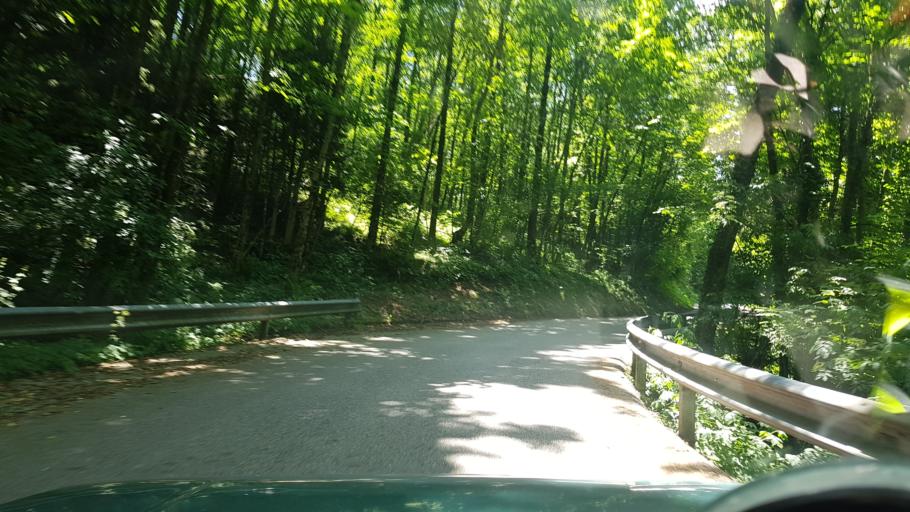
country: IT
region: Friuli Venezia Giulia
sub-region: Provincia di Udine
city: Lusevera
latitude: 46.2563
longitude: 13.2812
